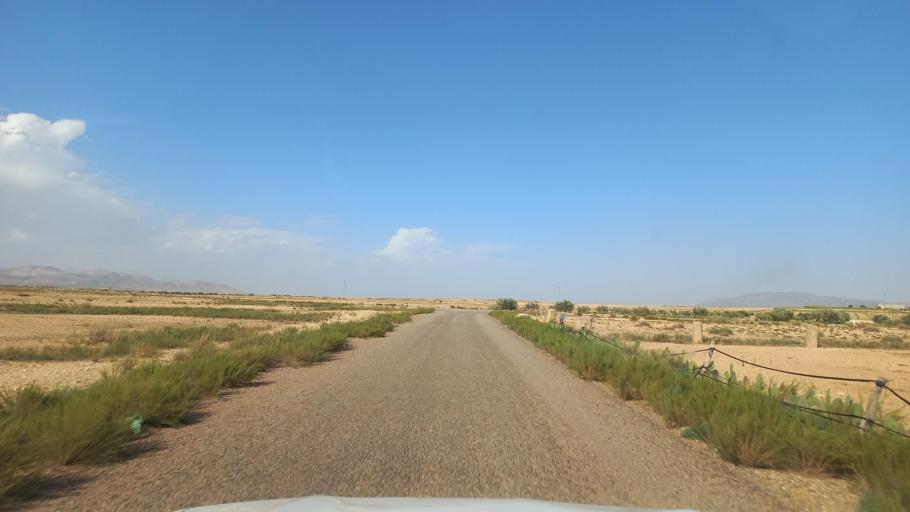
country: TN
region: Al Qasrayn
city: Sbiba
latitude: 35.3197
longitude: 9.0158
